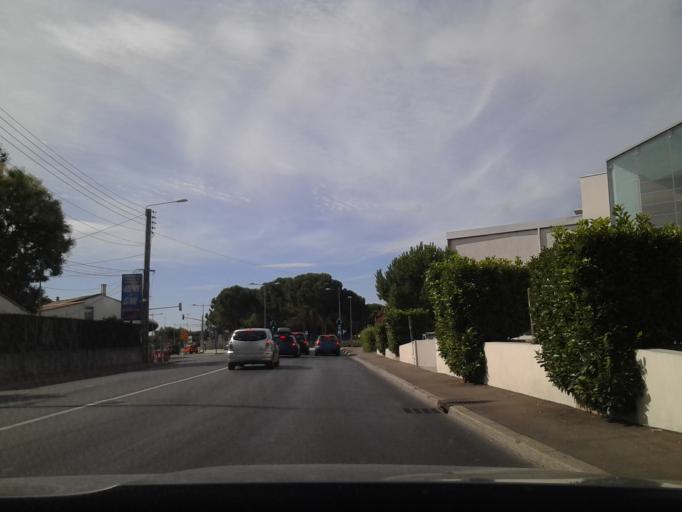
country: FR
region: Languedoc-Roussillon
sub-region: Departement de l'Herault
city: Montpellier
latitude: 43.5920
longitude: 3.8898
